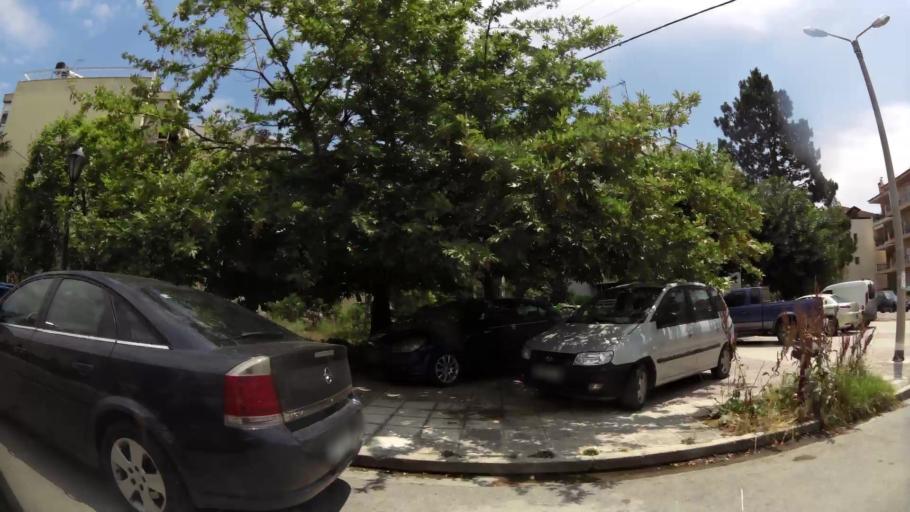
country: GR
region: Central Macedonia
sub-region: Nomos Pierias
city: Katerini
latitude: 40.2729
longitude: 22.5200
